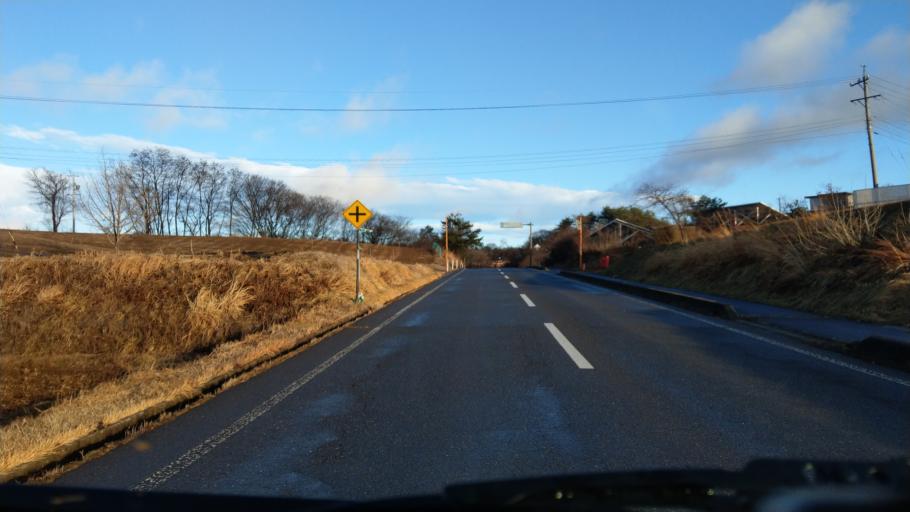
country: JP
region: Nagano
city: Komoro
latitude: 36.3048
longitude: 138.3742
